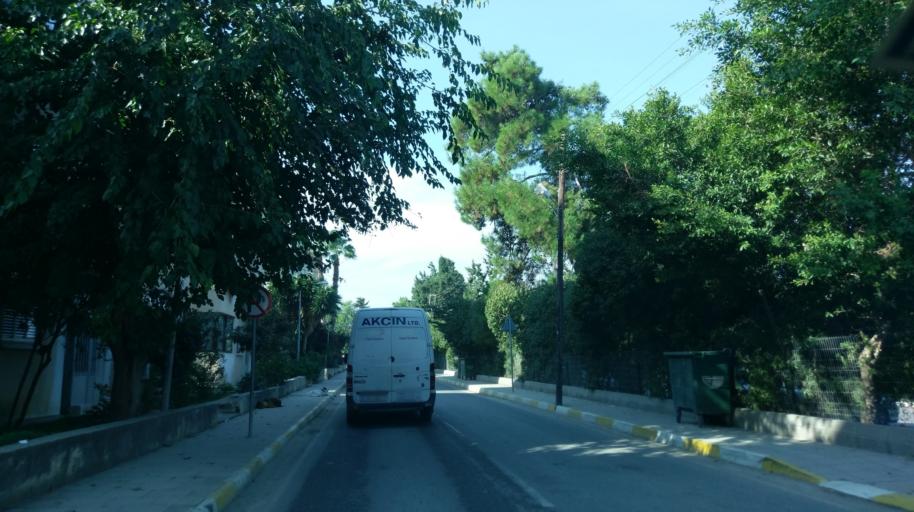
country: CY
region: Keryneia
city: Kyrenia
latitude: 35.3373
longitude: 33.3041
